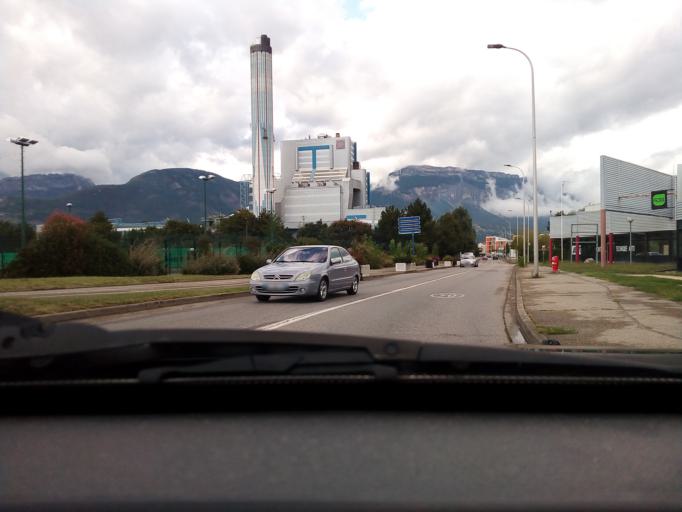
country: FR
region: Rhone-Alpes
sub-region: Departement de l'Isere
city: Saint-Martin-d'Heres
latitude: 45.1715
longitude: 5.7515
